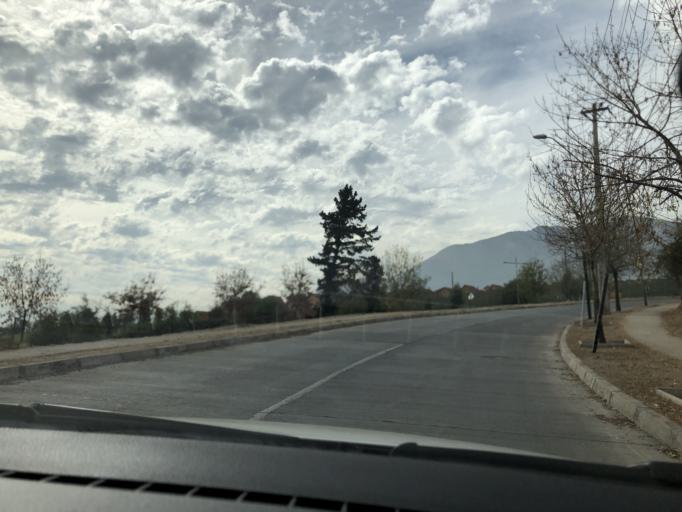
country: CL
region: Santiago Metropolitan
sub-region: Provincia de Cordillera
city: Puente Alto
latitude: -33.5879
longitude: -70.5357
